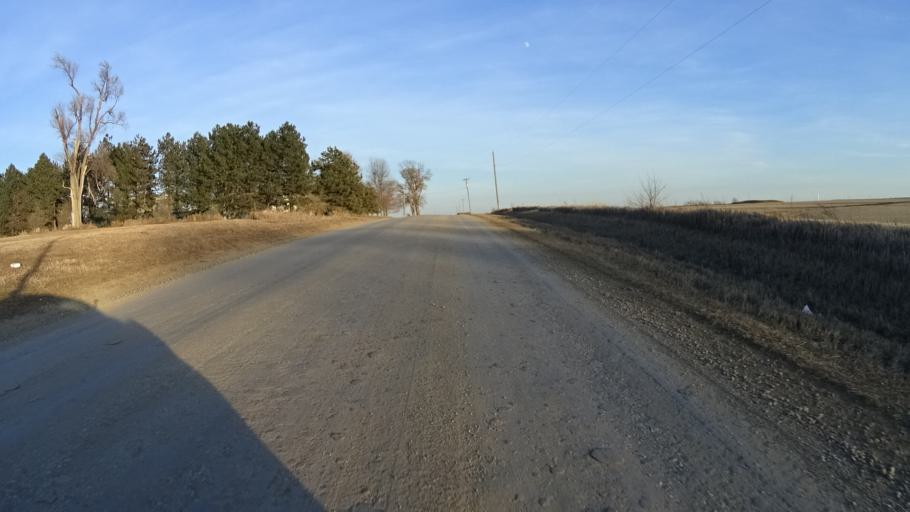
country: US
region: Nebraska
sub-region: Sarpy County
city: Springfield
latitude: 41.1326
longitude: -96.1054
